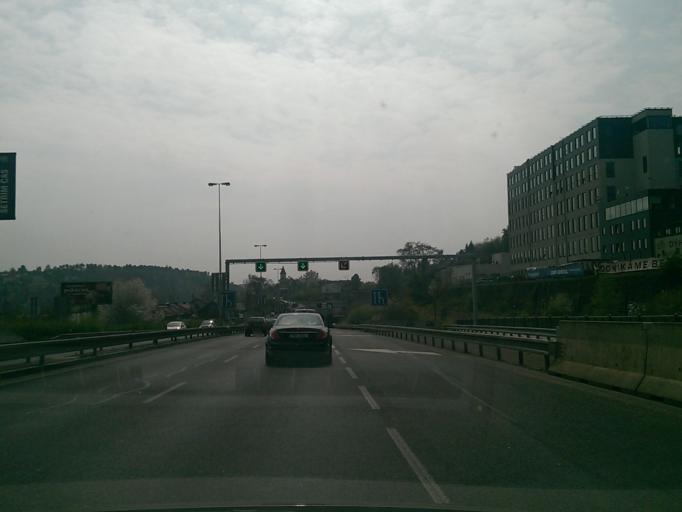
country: CZ
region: Praha
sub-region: Praha 2
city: Vysehrad
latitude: 50.0530
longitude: 14.4077
